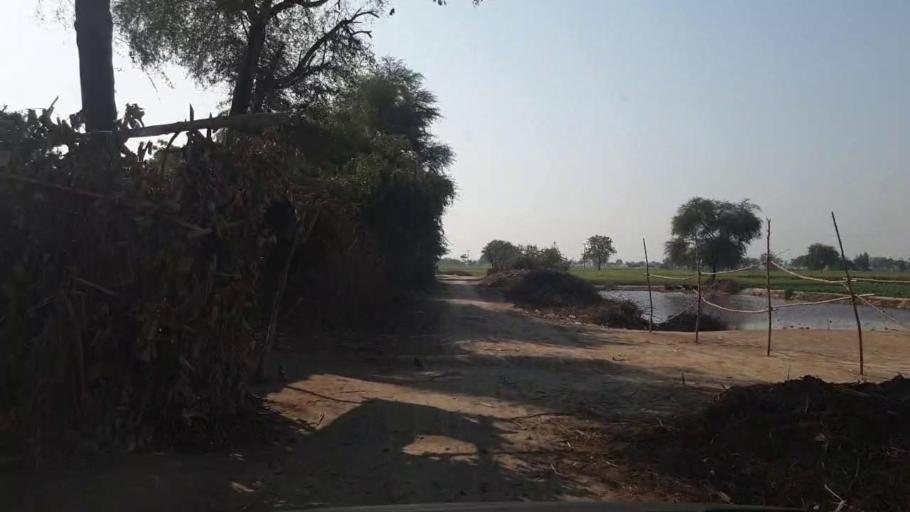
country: PK
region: Sindh
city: Bhit Shah
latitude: 25.7452
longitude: 68.5607
